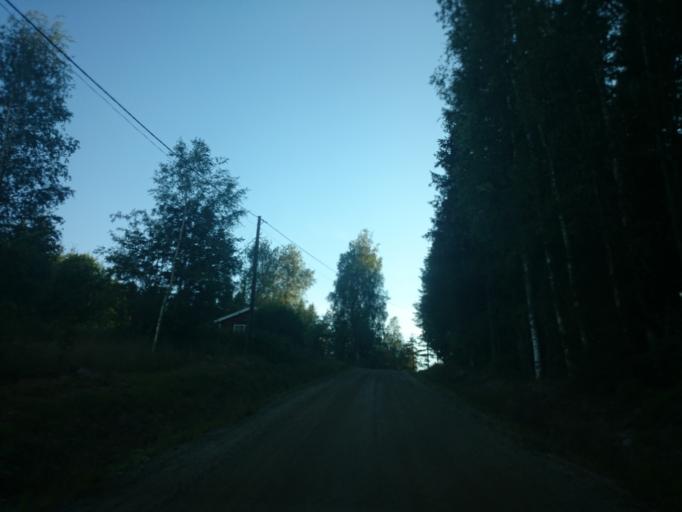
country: SE
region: Vaesternorrland
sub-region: Kramfors Kommun
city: Bollstabruk
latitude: 63.0518
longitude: 17.7190
